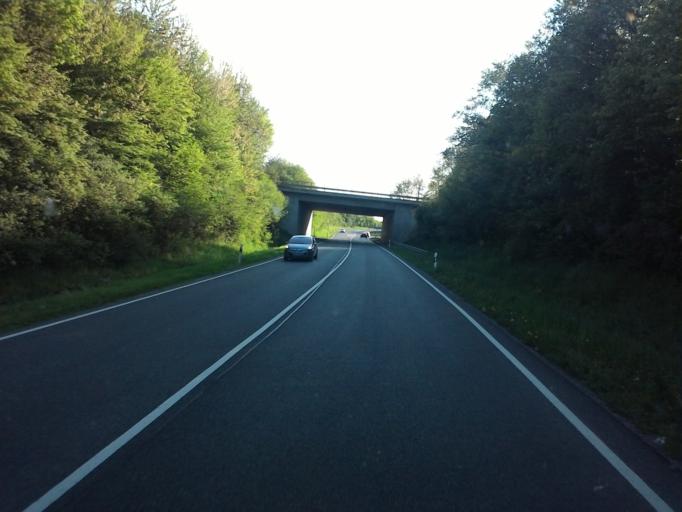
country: DE
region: Bavaria
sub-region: Regierungsbezirk Mittelfranken
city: Gallmersgarten
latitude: 49.4480
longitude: 10.2517
